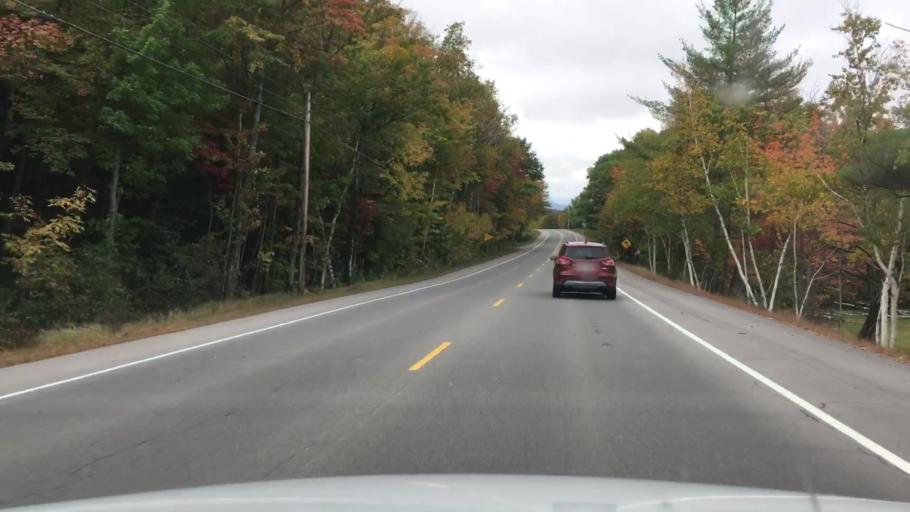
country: US
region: New Hampshire
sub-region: Coos County
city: Gorham
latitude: 44.3955
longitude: -71.1213
